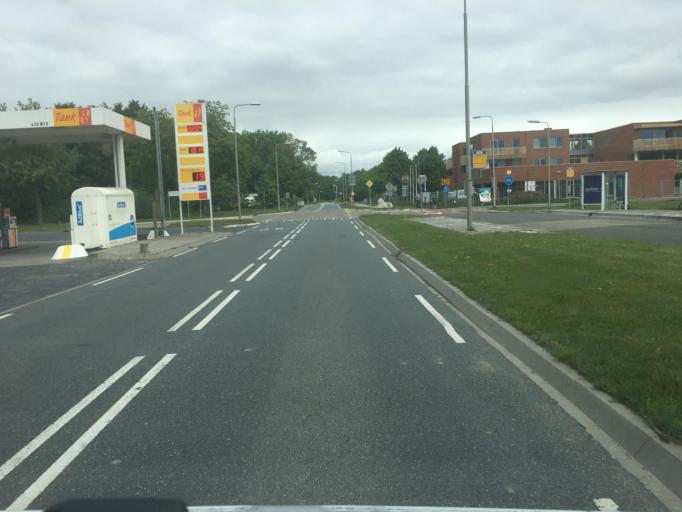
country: NL
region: Flevoland
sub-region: Gemeente Noordoostpolder
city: Emmeloord
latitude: 52.6439
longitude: 5.7219
